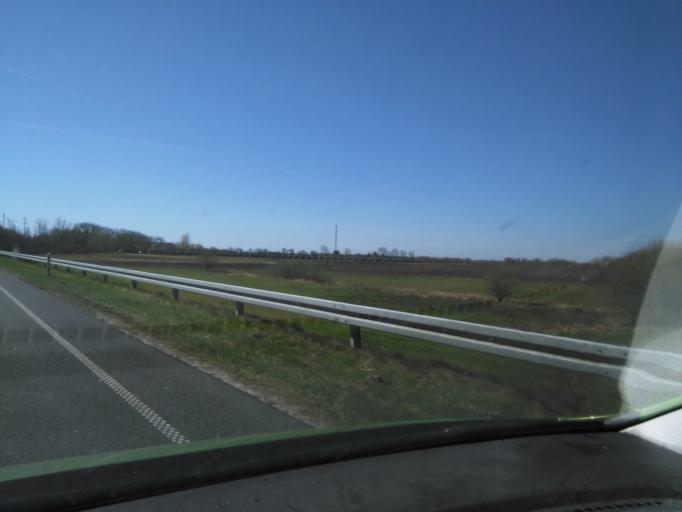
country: DK
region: South Denmark
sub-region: Varde Kommune
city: Varde
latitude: 55.6687
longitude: 8.5701
